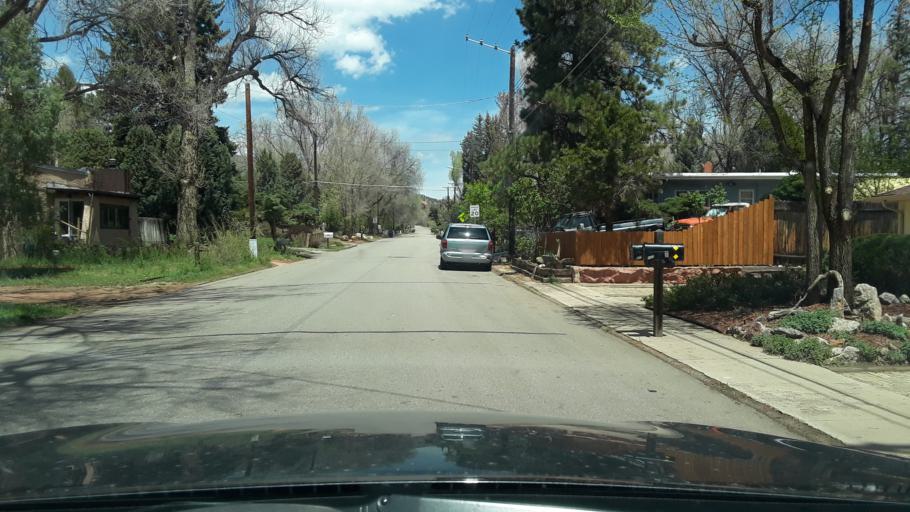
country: US
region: Colorado
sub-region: El Paso County
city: Manitou Springs
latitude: 38.8620
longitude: -104.8847
